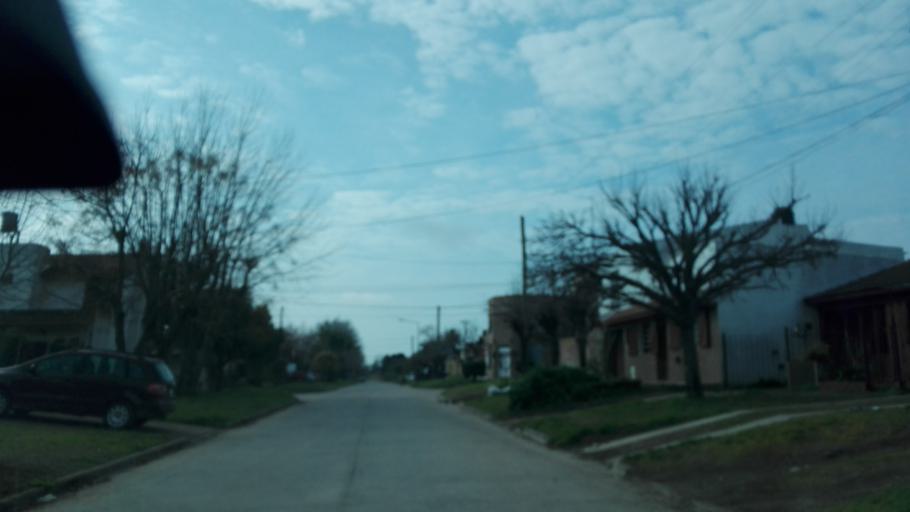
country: AR
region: Buenos Aires
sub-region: Partido de Chascomus
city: Chascomus
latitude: -35.5794
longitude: -58.0024
